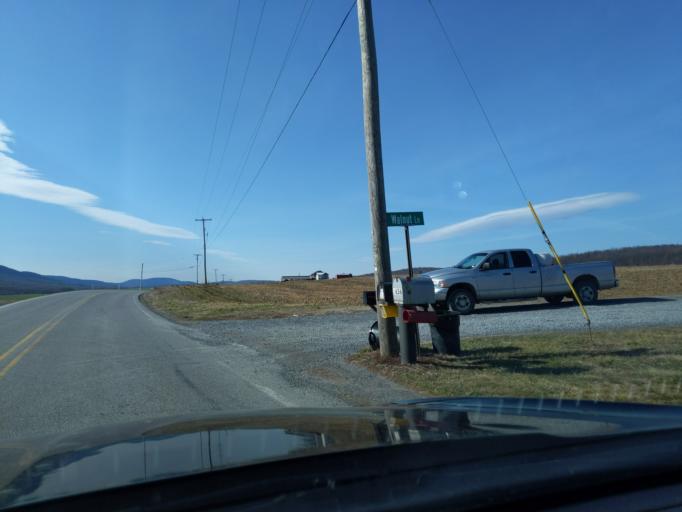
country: US
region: Pennsylvania
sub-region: Blair County
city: Martinsburg
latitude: 40.3556
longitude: -78.2512
